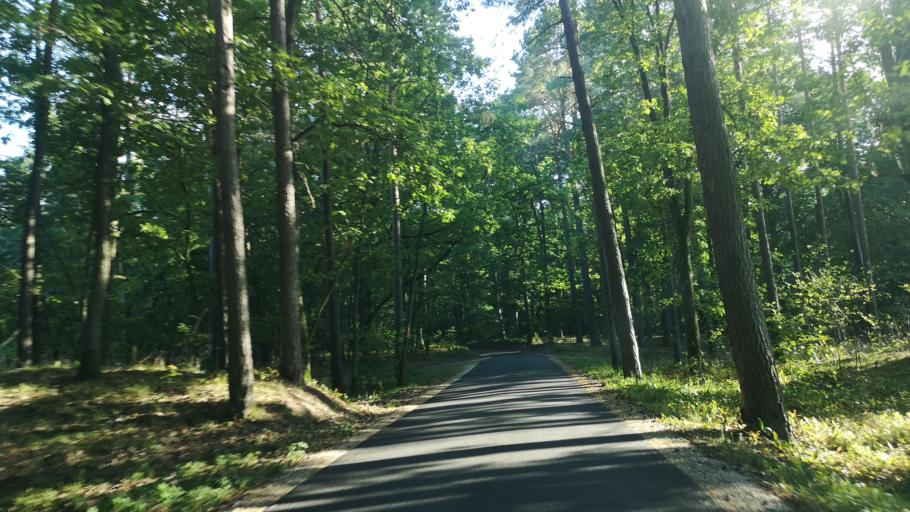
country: PL
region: Kujawsko-Pomorskie
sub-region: Powiat swiecki
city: Warlubie
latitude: 53.4781
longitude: 18.6316
